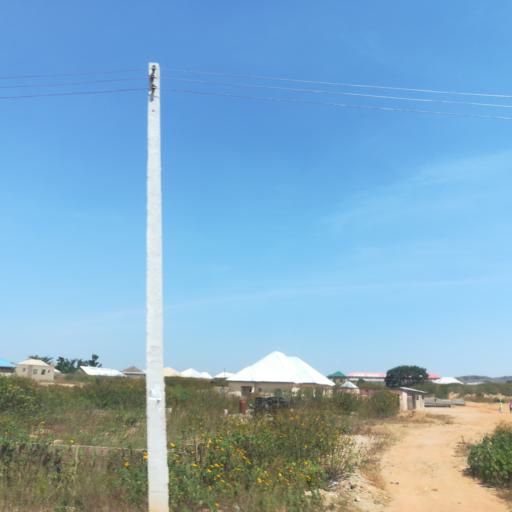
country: NG
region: Plateau
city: Jos
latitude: 9.8631
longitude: 8.9289
